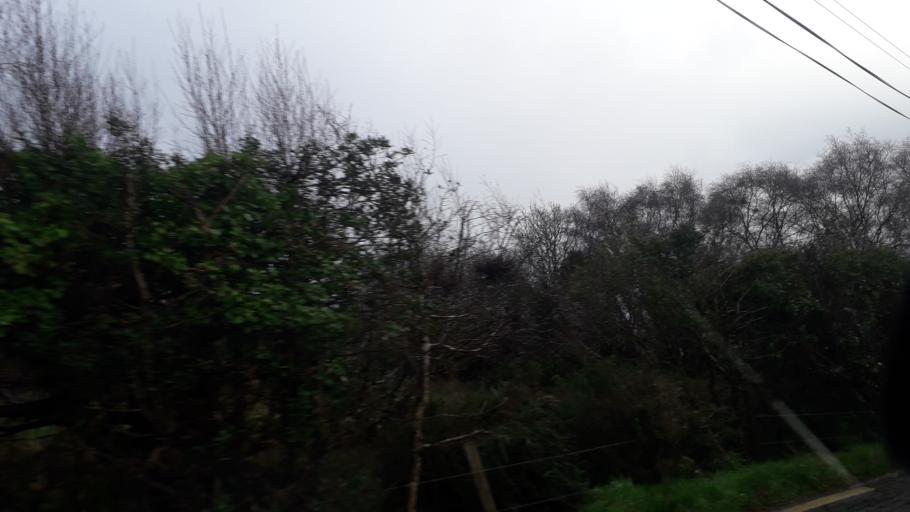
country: IE
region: Ulster
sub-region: County Donegal
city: Buncrana
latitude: 55.1314
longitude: -7.5295
